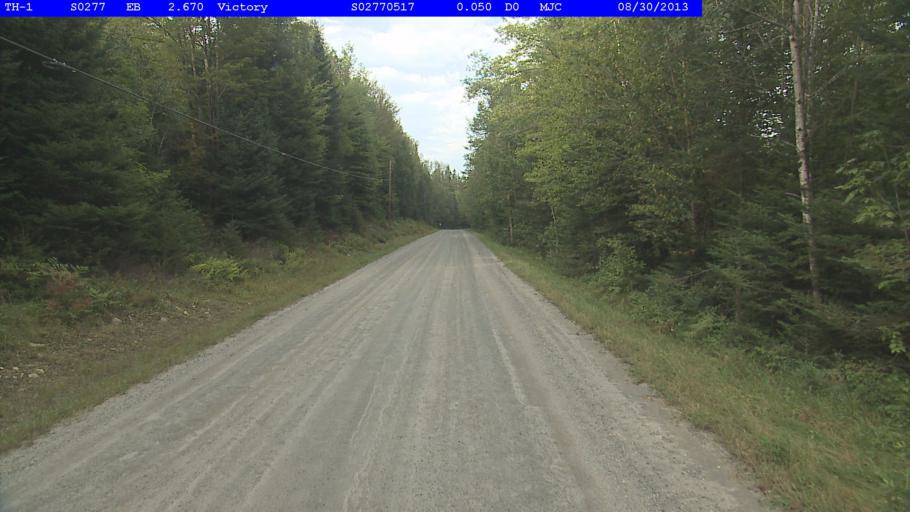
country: US
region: Vermont
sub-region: Caledonia County
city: Lyndonville
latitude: 44.4968
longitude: -71.8546
